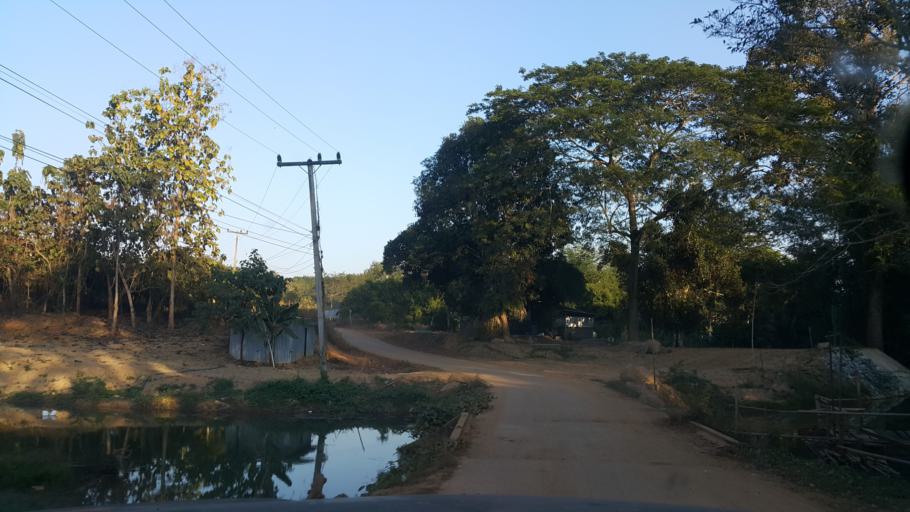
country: TH
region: Sukhothai
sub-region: Amphoe Si Satchanalai
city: Si Satchanalai
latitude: 17.6202
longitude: 99.6251
